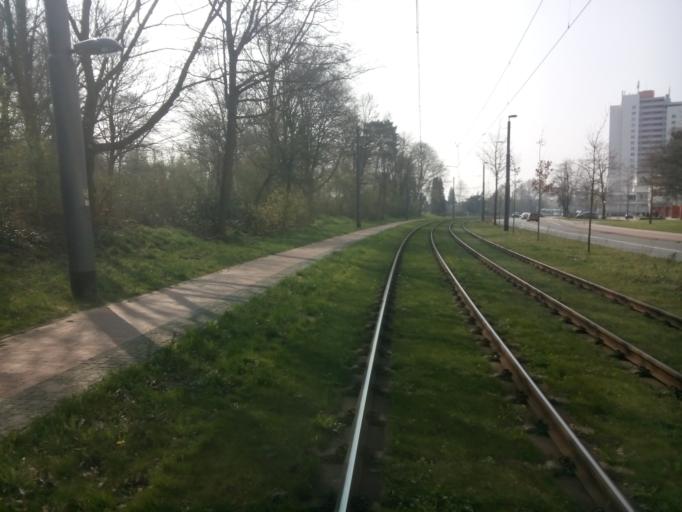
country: DE
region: Lower Saxony
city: Oyten
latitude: 53.0639
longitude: 8.9646
